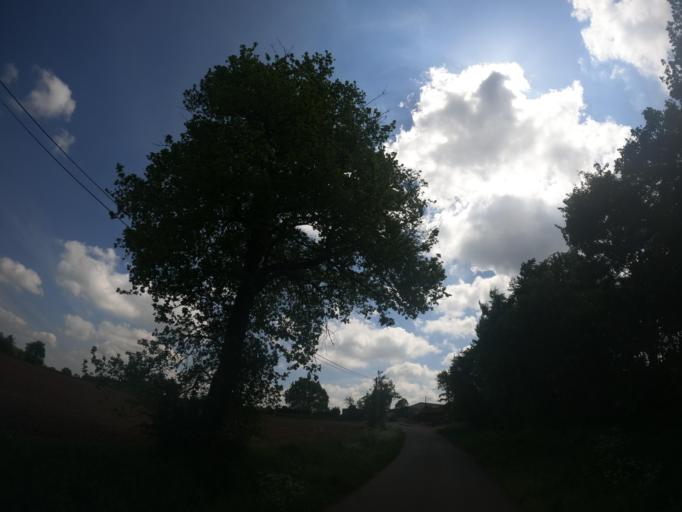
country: FR
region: Poitou-Charentes
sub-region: Departement des Deux-Sevres
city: Saint-Varent
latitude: 46.8492
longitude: -0.2262
